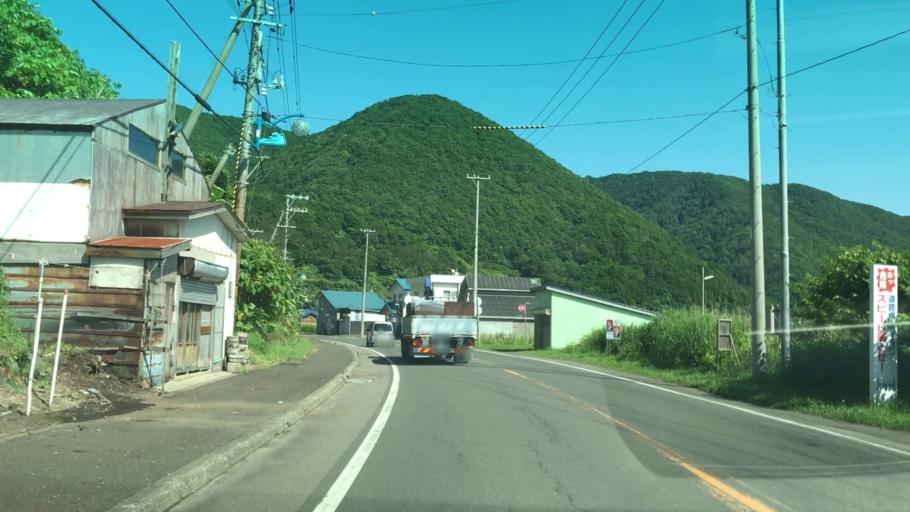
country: JP
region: Hokkaido
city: Iwanai
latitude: 43.1068
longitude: 140.4549
